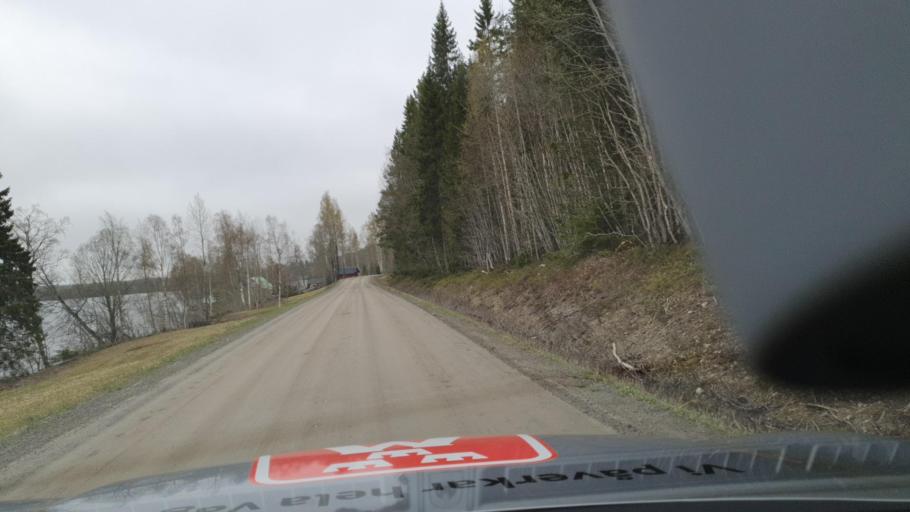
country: SE
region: Vaesternorrland
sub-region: OErnskoeldsviks Kommun
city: Husum
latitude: 63.6415
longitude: 19.0575
